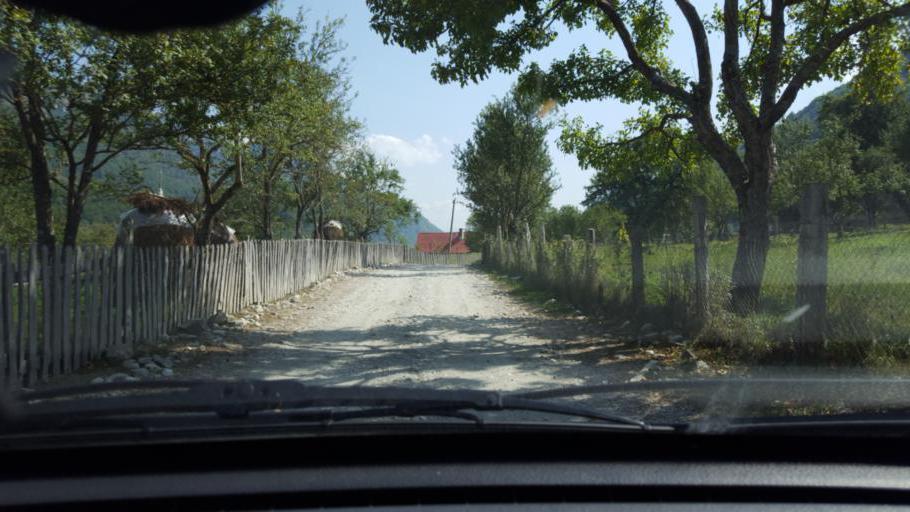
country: ME
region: Andrijevica
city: Andrijevica
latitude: 42.5905
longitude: 19.6898
